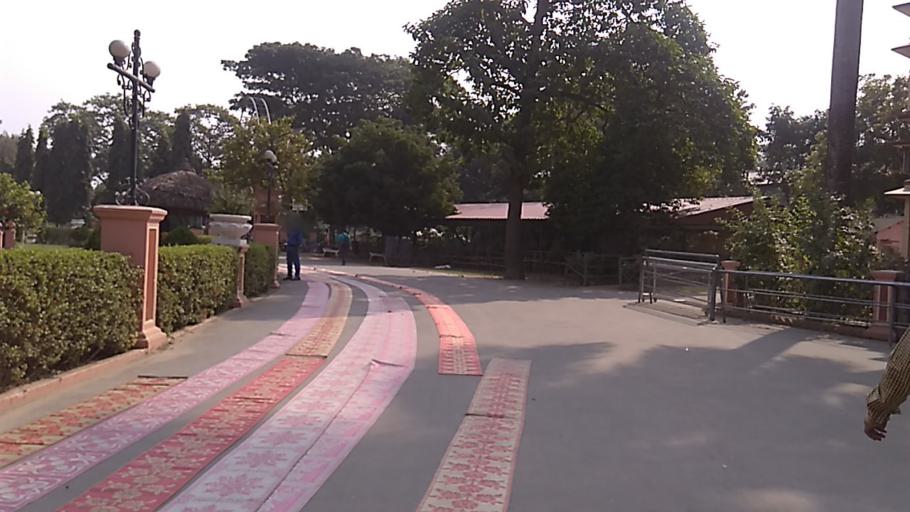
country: IN
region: West Bengal
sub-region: Nadia
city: Navadwip
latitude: 23.4233
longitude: 88.3875
